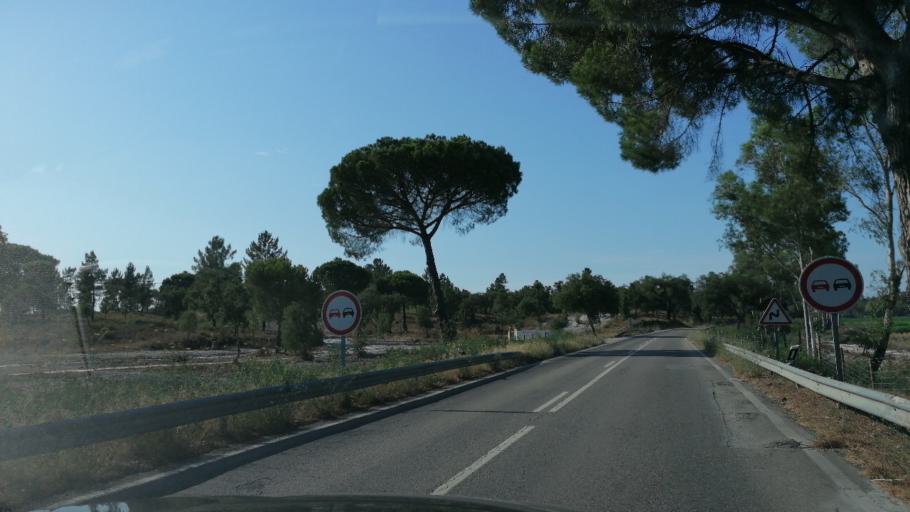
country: PT
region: Santarem
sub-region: Coruche
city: Coruche
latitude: 38.9933
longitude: -8.5546
